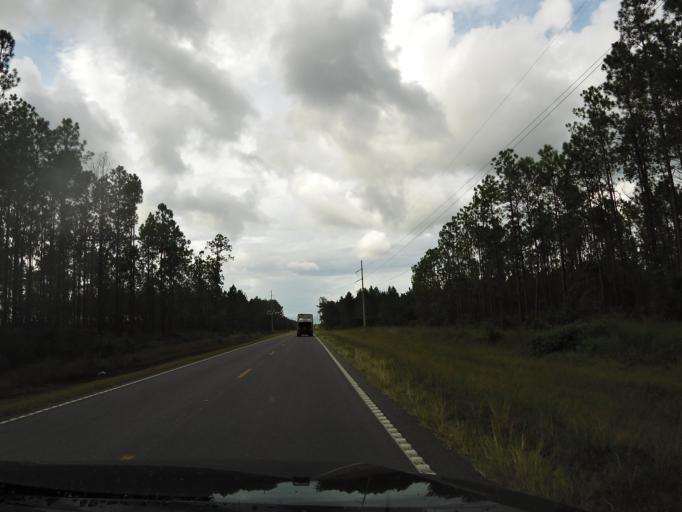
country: US
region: Florida
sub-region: Nassau County
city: Hilliard
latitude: 30.5899
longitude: -82.0479
